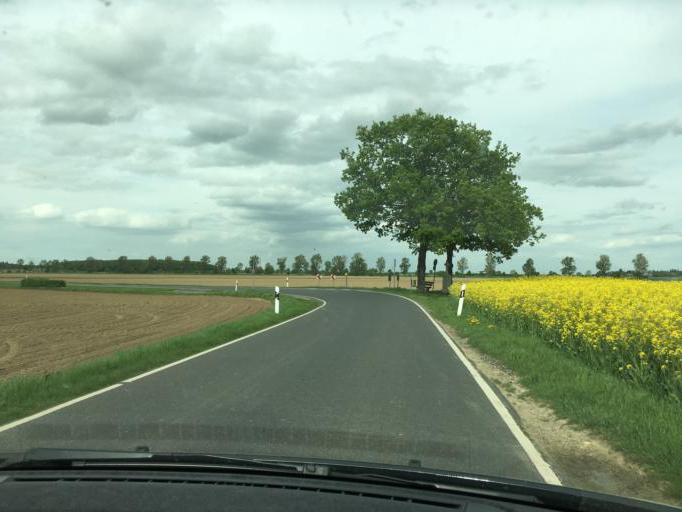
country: DE
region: North Rhine-Westphalia
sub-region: Regierungsbezirk Koln
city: Merzenich
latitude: 50.7882
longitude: 6.5481
